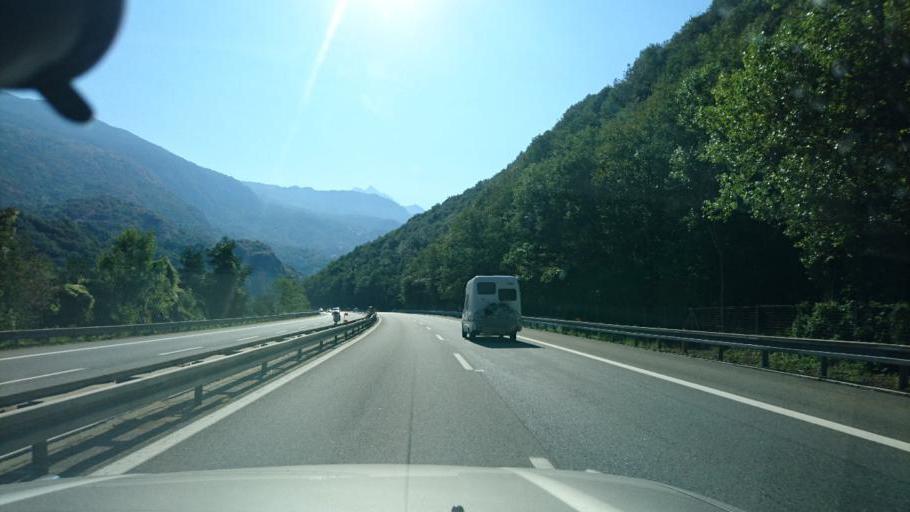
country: IT
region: Aosta Valley
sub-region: Valle d'Aosta
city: Saint-Vincent
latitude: 45.7414
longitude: 7.6405
